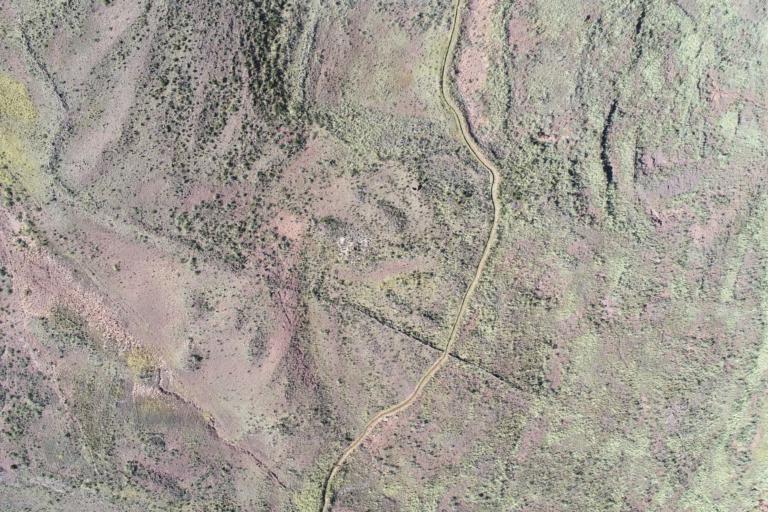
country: BO
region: La Paz
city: Tiahuanaco
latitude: -16.6033
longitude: -68.7575
